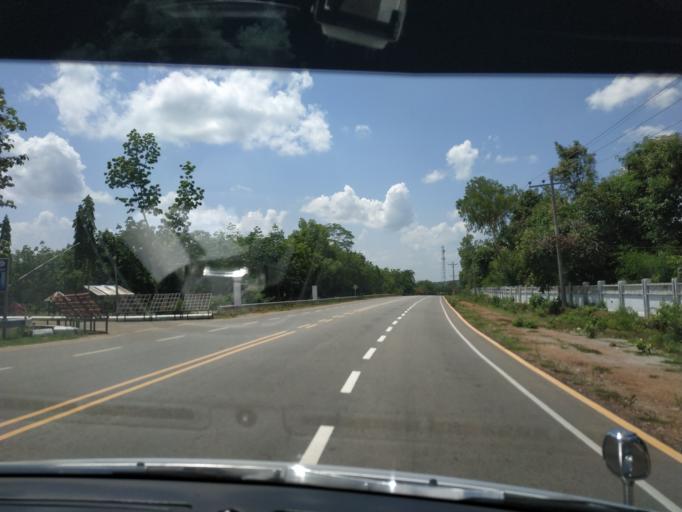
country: MM
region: Mon
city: Kyaikto
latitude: 17.3402
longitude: 97.0381
